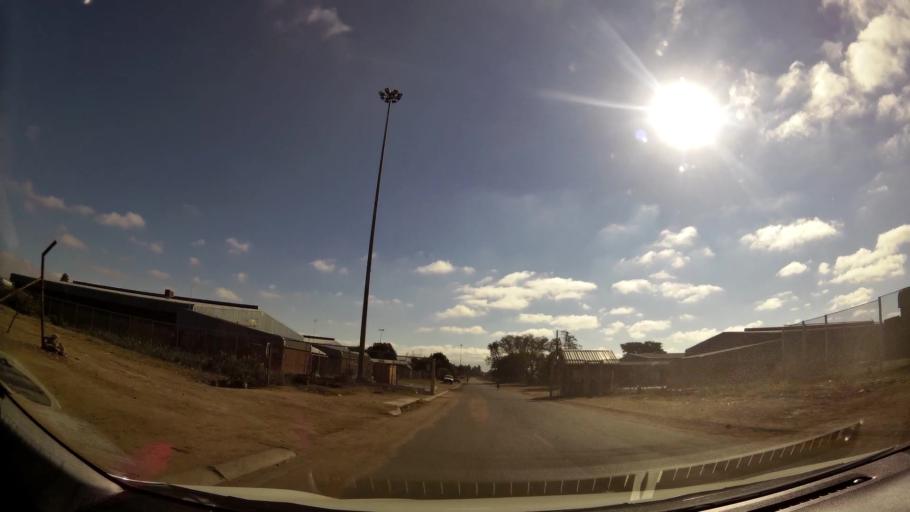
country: ZA
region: Limpopo
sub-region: Capricorn District Municipality
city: Polokwane
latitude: -23.8463
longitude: 29.4002
